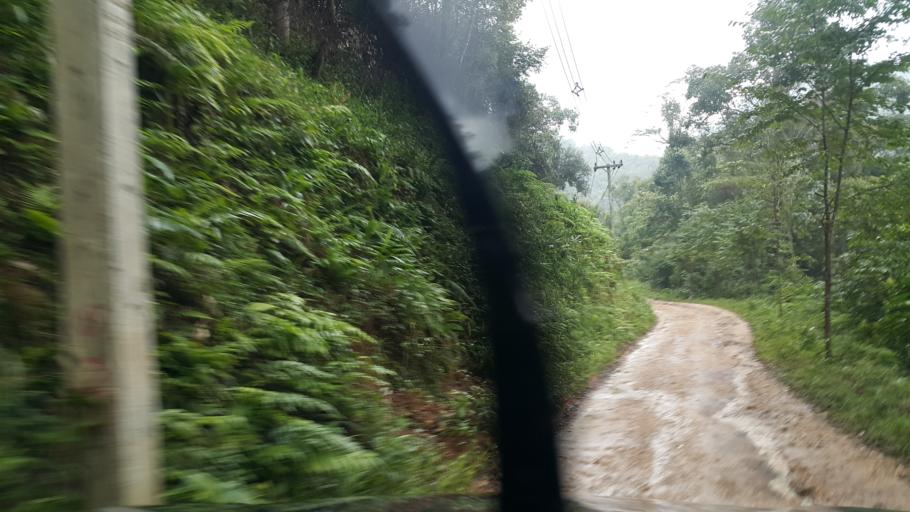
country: TH
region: Lampang
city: Wang Nuea
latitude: 19.1323
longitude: 99.3589
